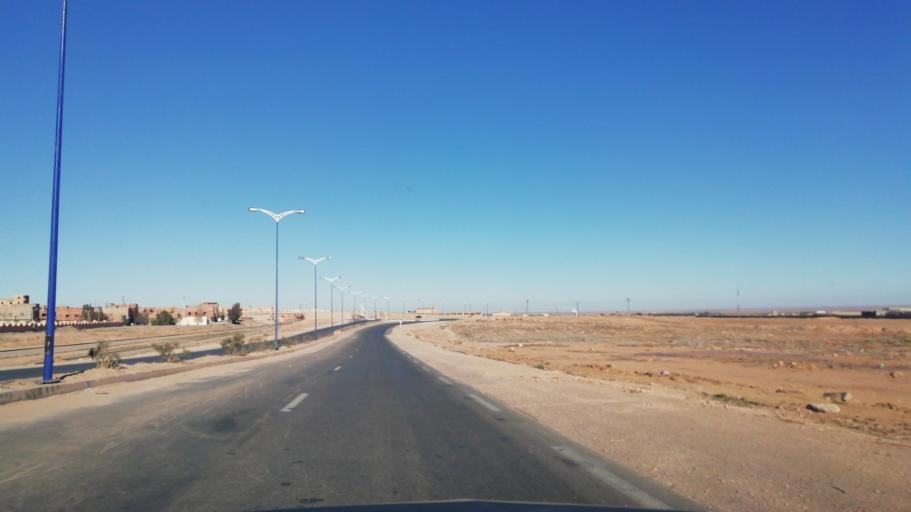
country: DZ
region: Wilaya de Naama
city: Naama
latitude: 33.5378
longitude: -0.2625
